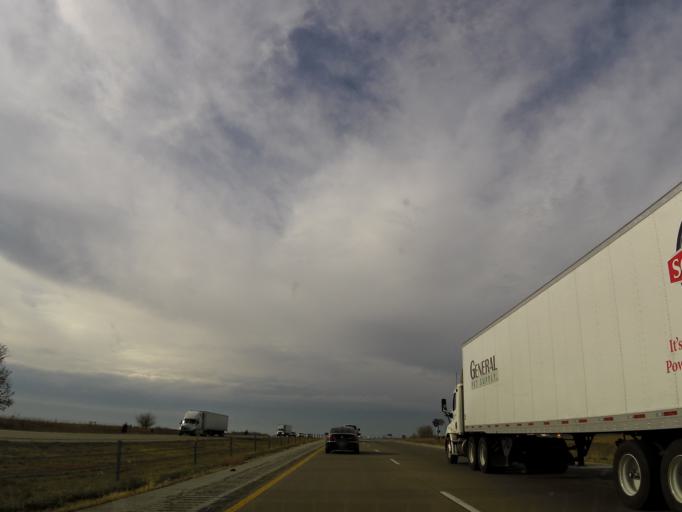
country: US
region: Iowa
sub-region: Scott County
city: Eldridge
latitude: 41.6001
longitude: -90.6272
